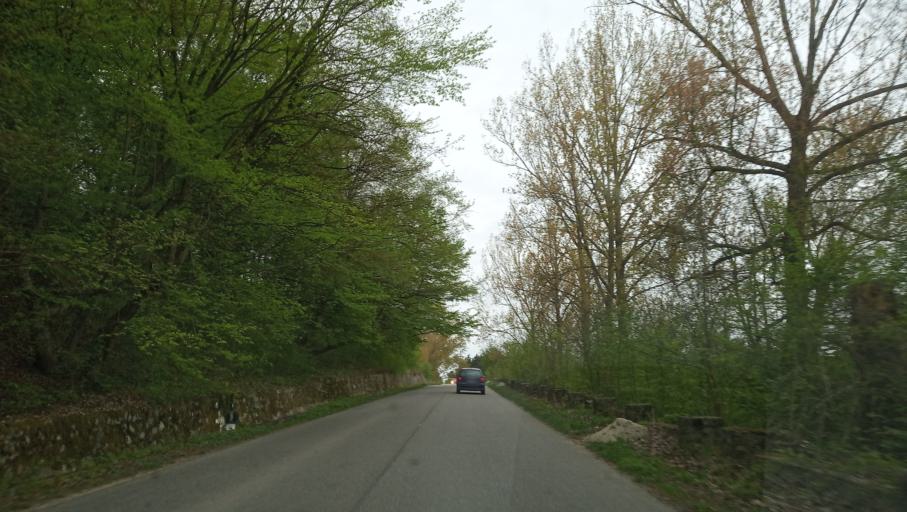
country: RO
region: Valcea
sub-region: Municipiul Ramnicu Valcea
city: Goranu
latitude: 45.1275
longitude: 24.3993
